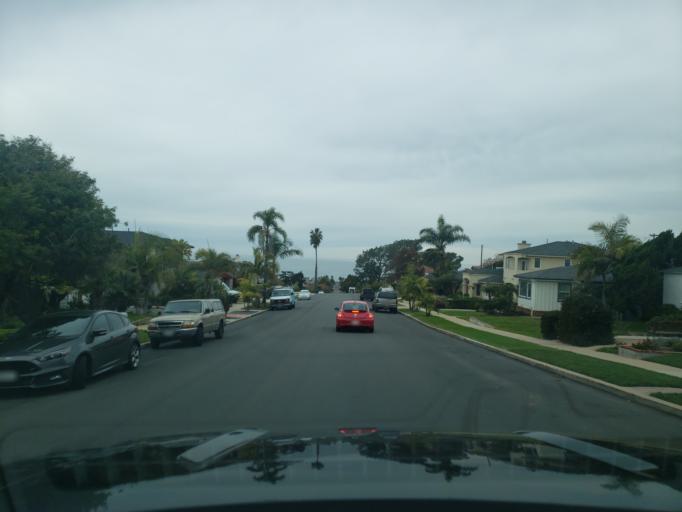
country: US
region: California
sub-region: San Diego County
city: Coronado
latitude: 32.7368
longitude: -117.2474
